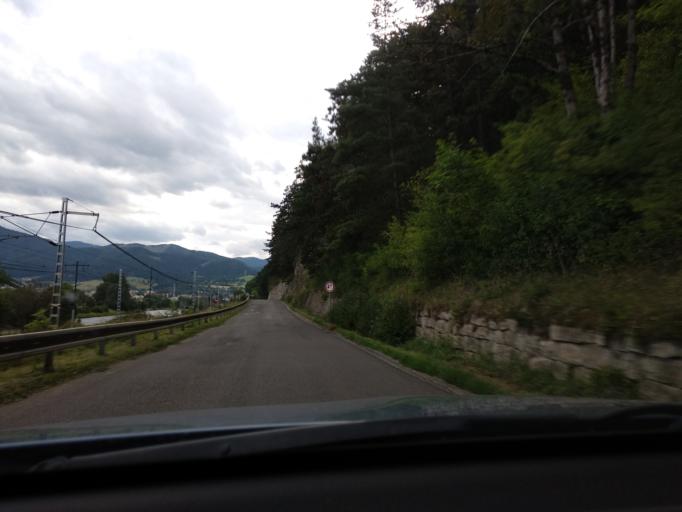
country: SK
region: Zilinsky
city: Ruzomberok
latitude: 49.0845
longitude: 19.3274
